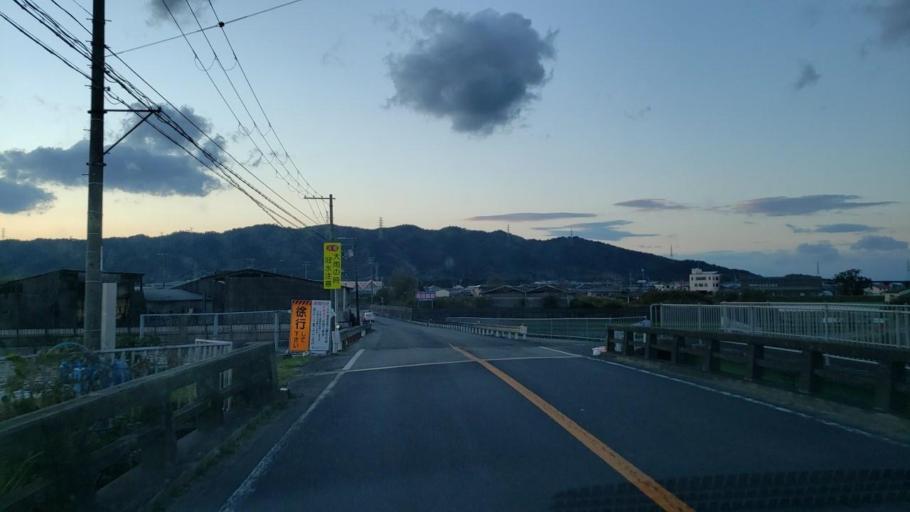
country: JP
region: Hyogo
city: Fukura
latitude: 34.3020
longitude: 134.7505
